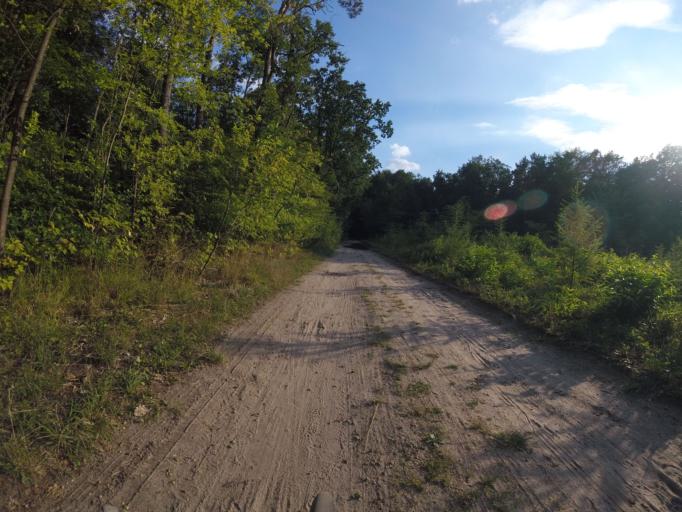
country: DE
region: Brandenburg
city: Petershagen
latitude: 52.5660
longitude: 13.8222
